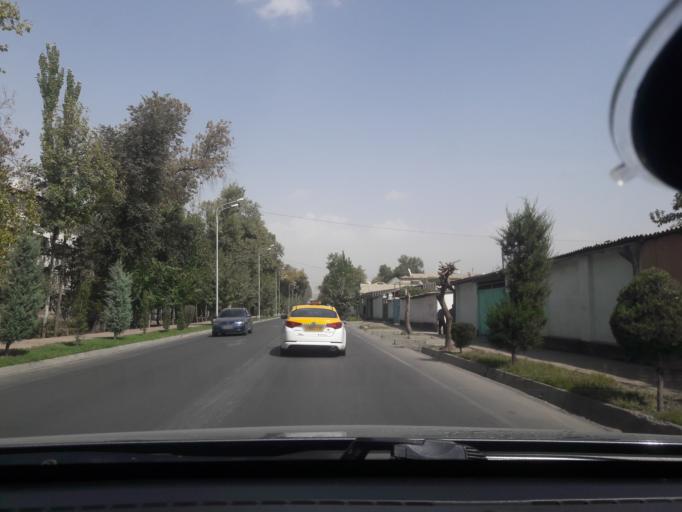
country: TJ
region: Dushanbe
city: Dushanbe
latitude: 38.5643
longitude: 68.7625
